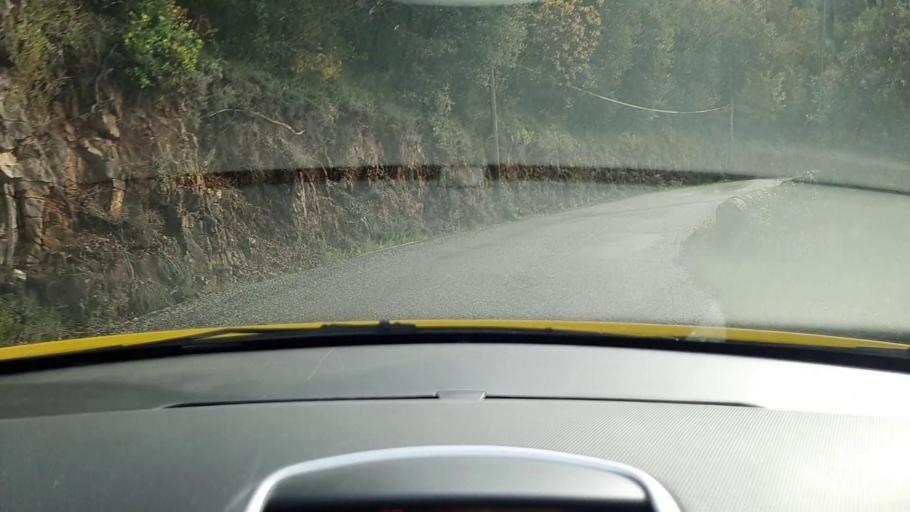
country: FR
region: Languedoc-Roussillon
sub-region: Departement du Gard
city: Saint-Jean-du-Gard
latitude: 44.0553
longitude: 3.9231
